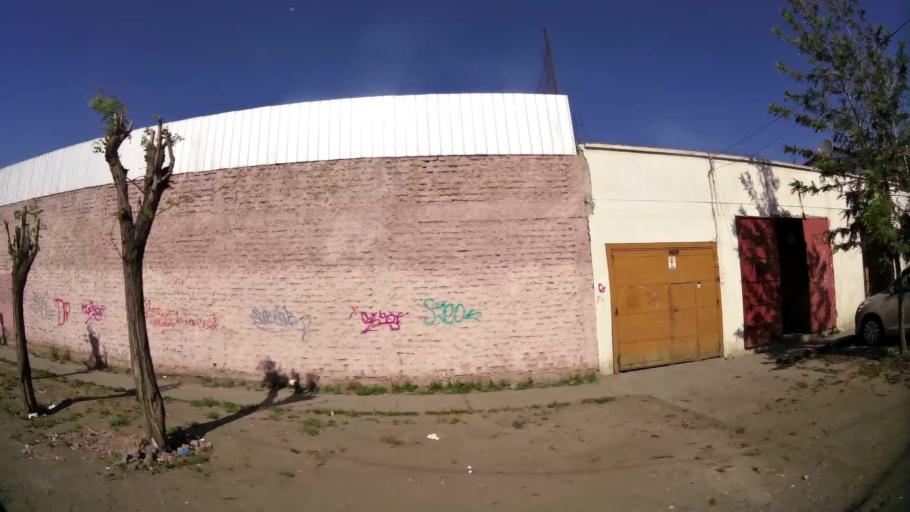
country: CL
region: Santiago Metropolitan
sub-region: Provincia de Santiago
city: Santiago
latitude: -33.5162
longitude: -70.6876
